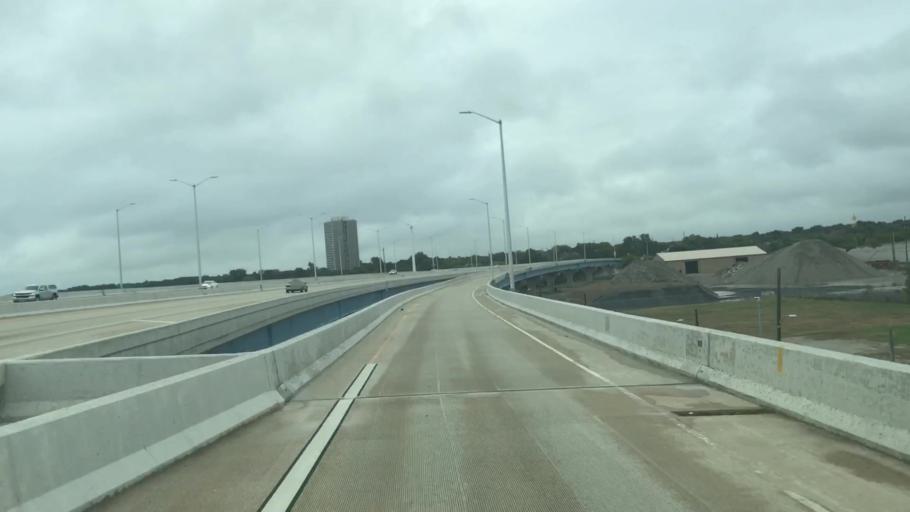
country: US
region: Wisconsin
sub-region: Milwaukee County
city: Milwaukee
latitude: 43.0079
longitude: -87.8925
